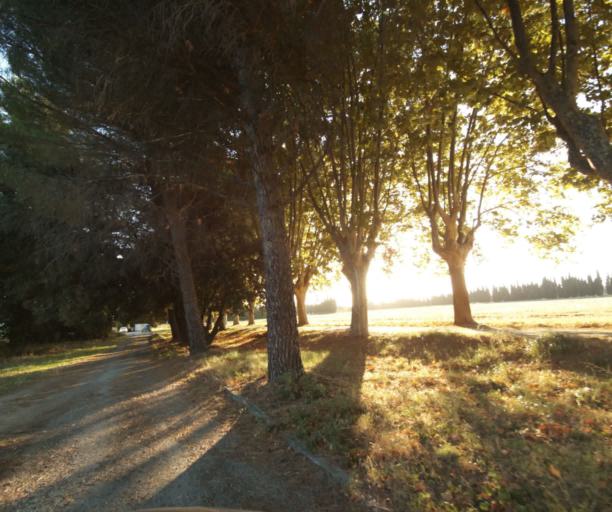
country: FR
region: Languedoc-Roussillon
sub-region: Departement du Gard
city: Bouillargues
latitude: 43.8062
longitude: 4.4045
